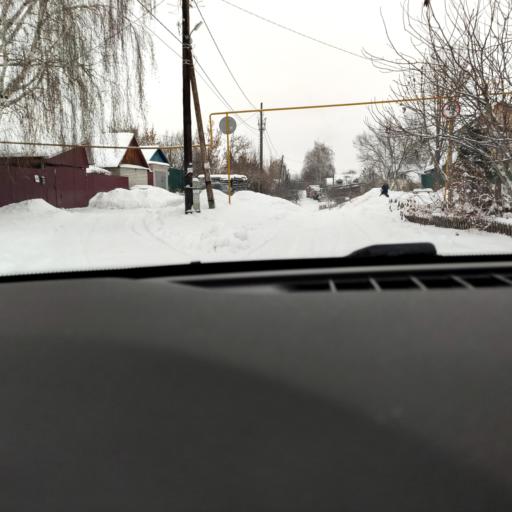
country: RU
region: Samara
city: Smyshlyayevka
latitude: 53.2428
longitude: 50.3455
